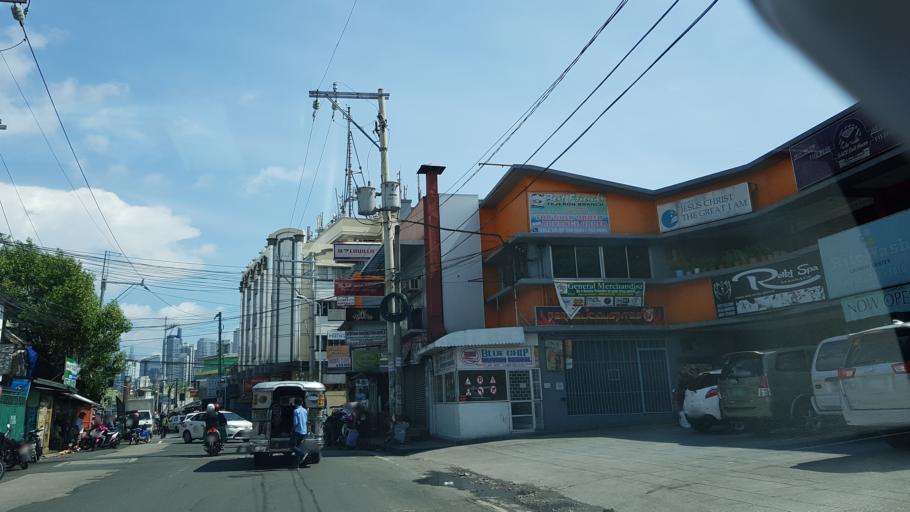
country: PH
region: Metro Manila
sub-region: Mandaluyong
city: Mandaluyong City
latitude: 14.5760
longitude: 121.0117
